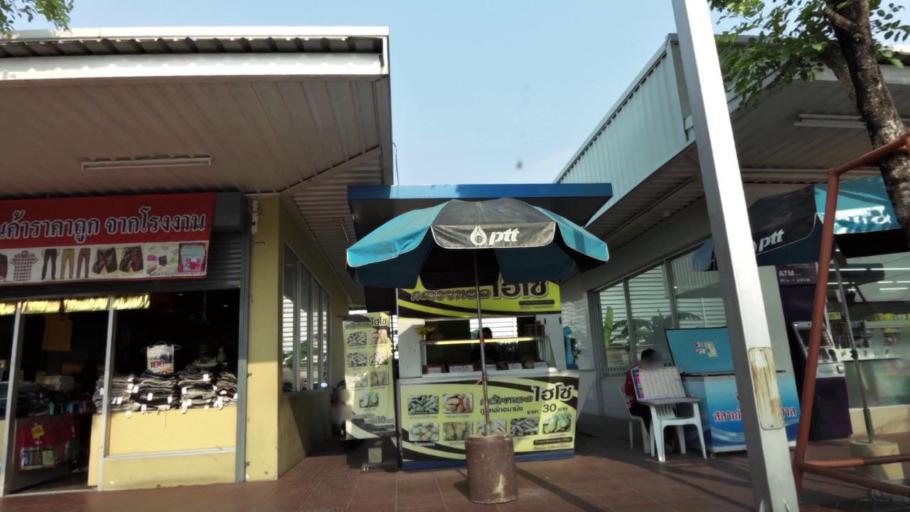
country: TH
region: Phra Nakhon Si Ayutthaya
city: Phra Nakhon Si Ayutthaya
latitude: 14.3261
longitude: 100.6250
